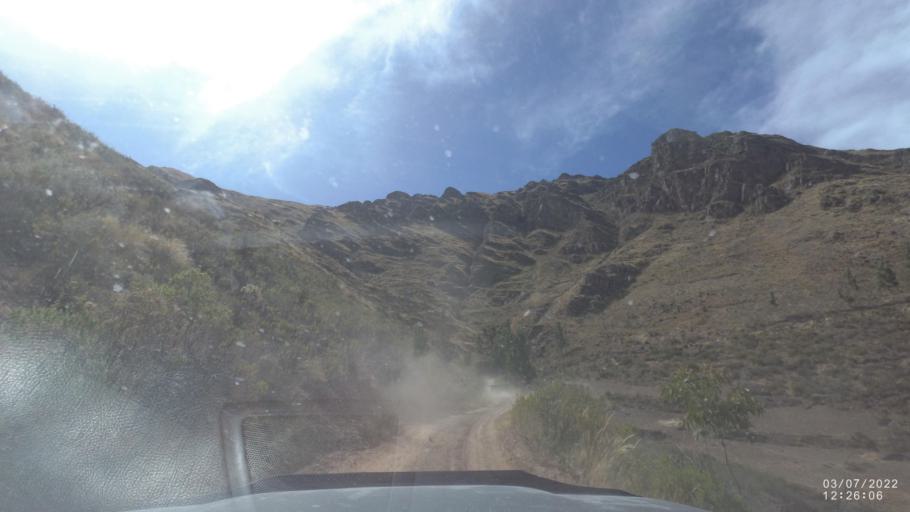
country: BO
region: Cochabamba
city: Irpa Irpa
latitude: -17.8090
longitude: -66.6173
